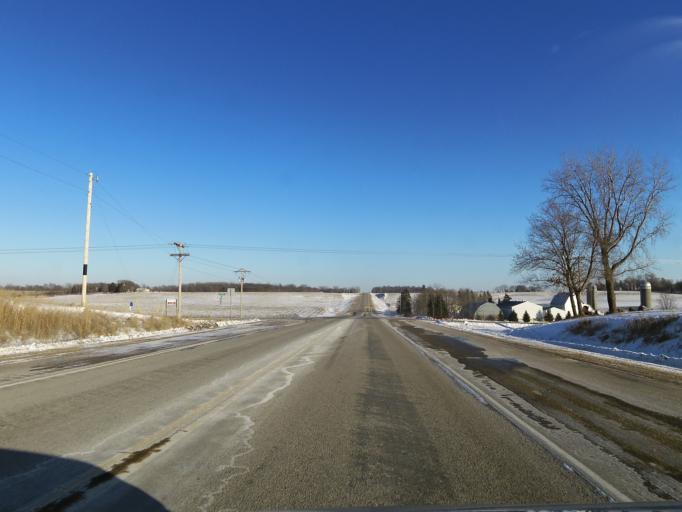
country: US
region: Minnesota
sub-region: Le Sueur County
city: Montgomery
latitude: 44.4861
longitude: -93.5255
